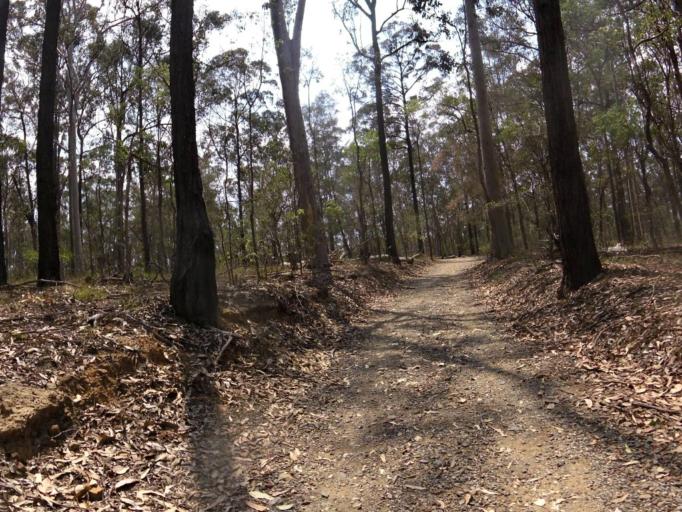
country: AU
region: Queensland
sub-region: Logan
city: Springwood
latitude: -27.6077
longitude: 153.1575
